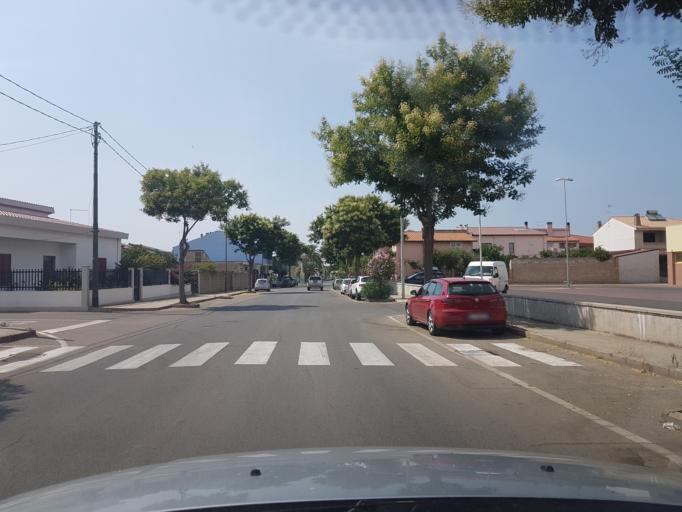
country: IT
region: Sardinia
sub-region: Provincia di Oristano
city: Cabras
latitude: 39.9237
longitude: 8.5400
